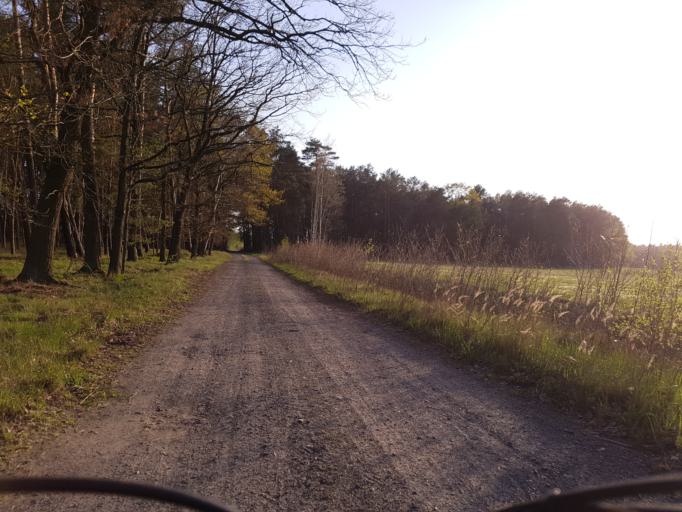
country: DE
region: Brandenburg
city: Schilda
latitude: 51.5962
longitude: 13.3677
